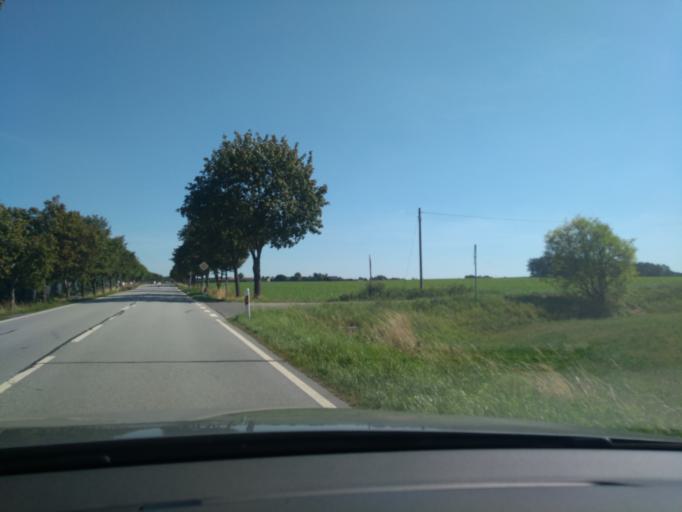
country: DE
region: Saxony
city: Goda
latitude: 51.1930
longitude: 14.3412
